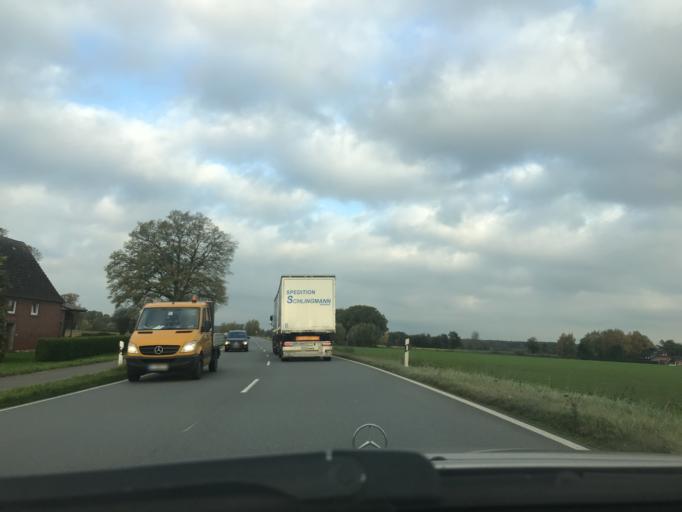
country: DE
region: North Rhine-Westphalia
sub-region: Regierungsbezirk Arnsberg
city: Soest
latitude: 51.6481
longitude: 8.0830
